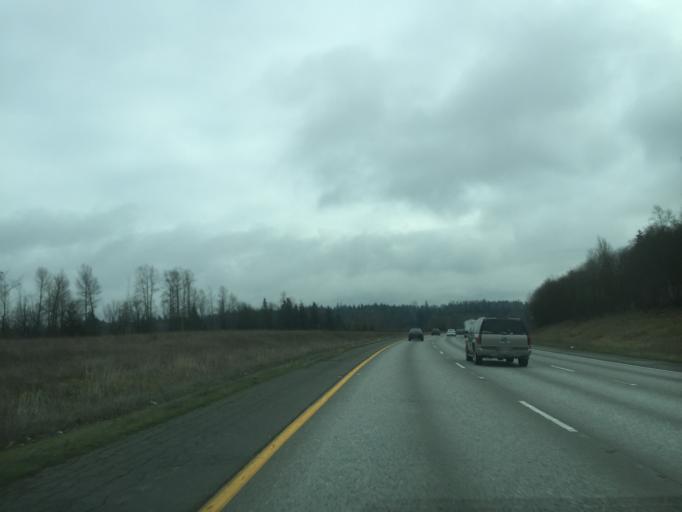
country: US
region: Washington
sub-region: Snohomish County
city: Bryant
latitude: 48.2237
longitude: -122.2236
